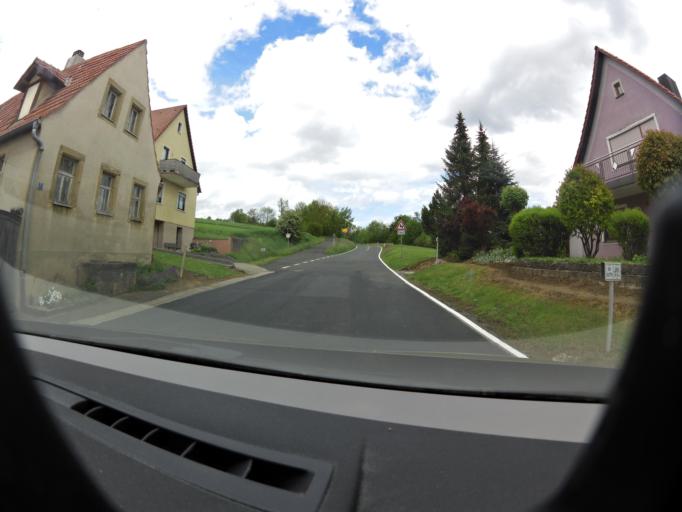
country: DE
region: Bavaria
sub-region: Regierungsbezirk Unterfranken
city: Dettelbach
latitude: 49.8311
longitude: 10.1481
